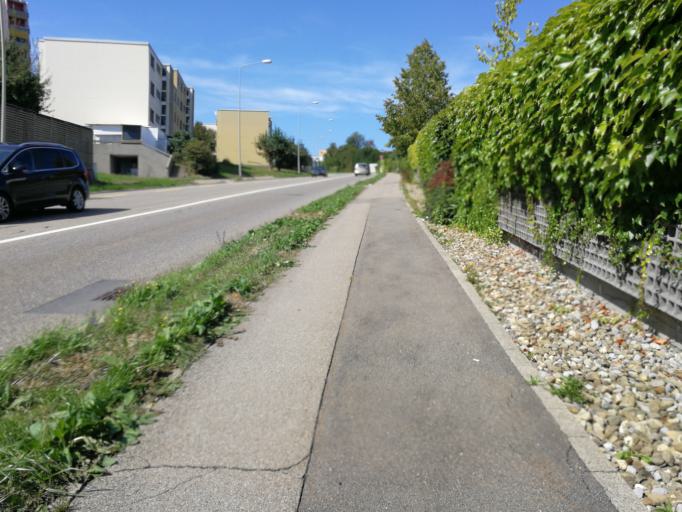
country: CH
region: Zurich
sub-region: Bezirk Horgen
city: Waedenswil / Hangenmoos
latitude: 47.2323
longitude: 8.6567
